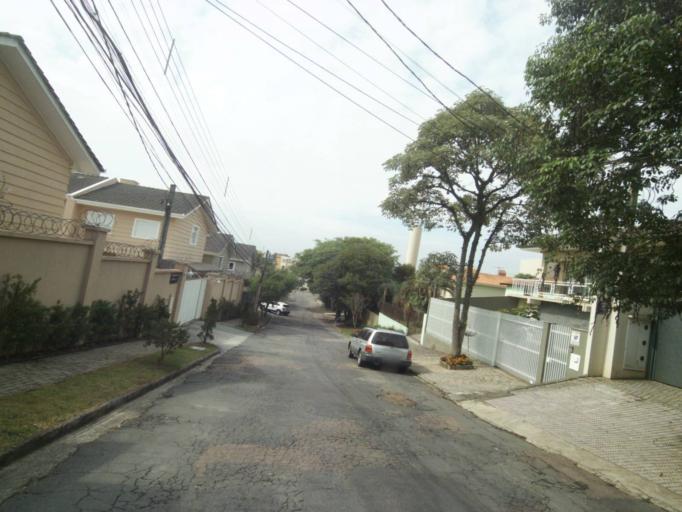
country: BR
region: Parana
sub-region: Curitiba
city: Curitiba
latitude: -25.4089
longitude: -49.2950
